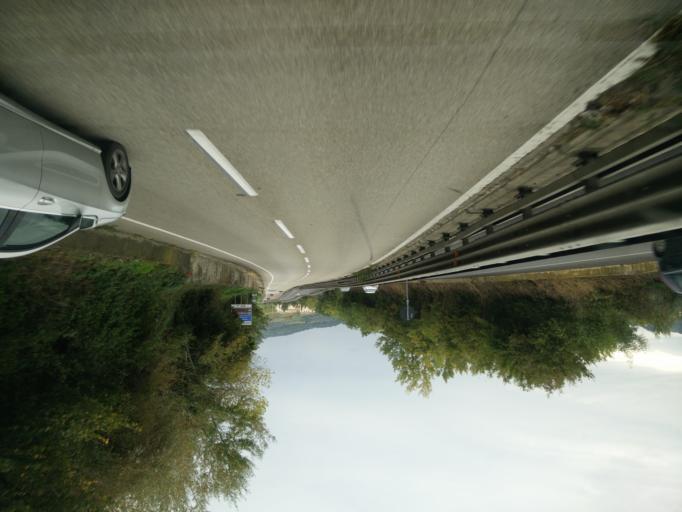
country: IT
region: Tuscany
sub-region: Provincia di Siena
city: Poggibonsi
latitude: 43.4825
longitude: 11.1504
